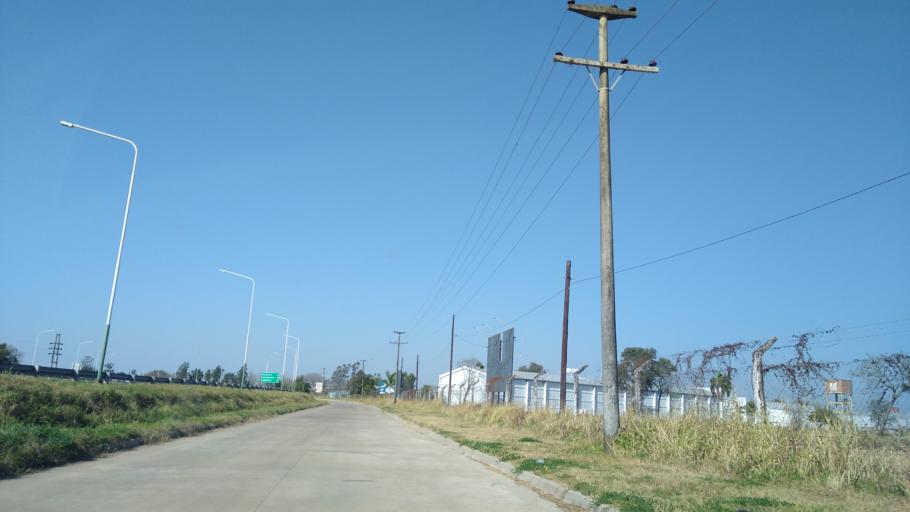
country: AR
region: Chaco
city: Puerto Tirol
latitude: -27.3631
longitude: -59.0615
